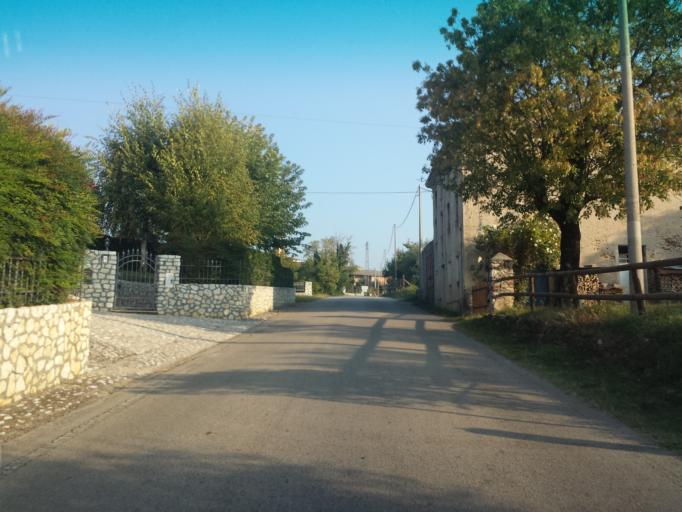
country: IT
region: Veneto
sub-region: Provincia di Vicenza
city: Mason Vicentino
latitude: 45.7255
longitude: 11.5843
